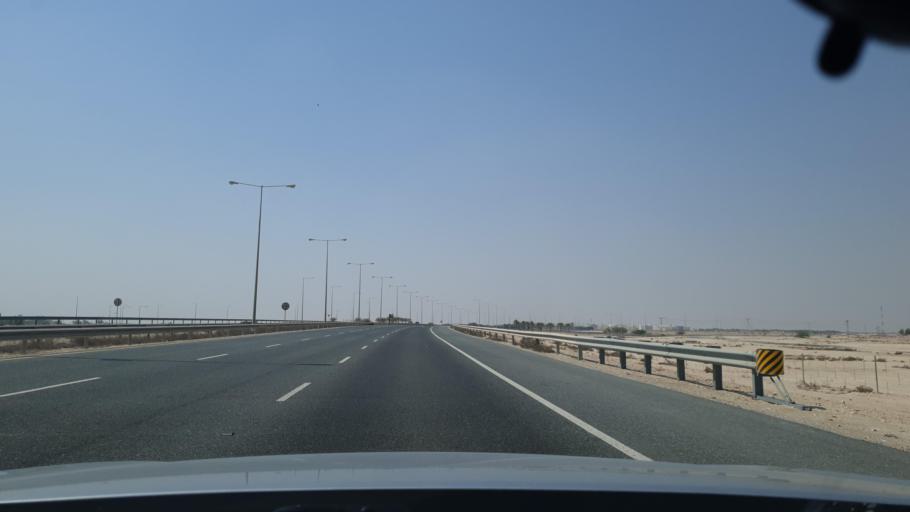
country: QA
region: Al Khawr
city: Al Khawr
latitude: 25.7540
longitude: 51.4419
